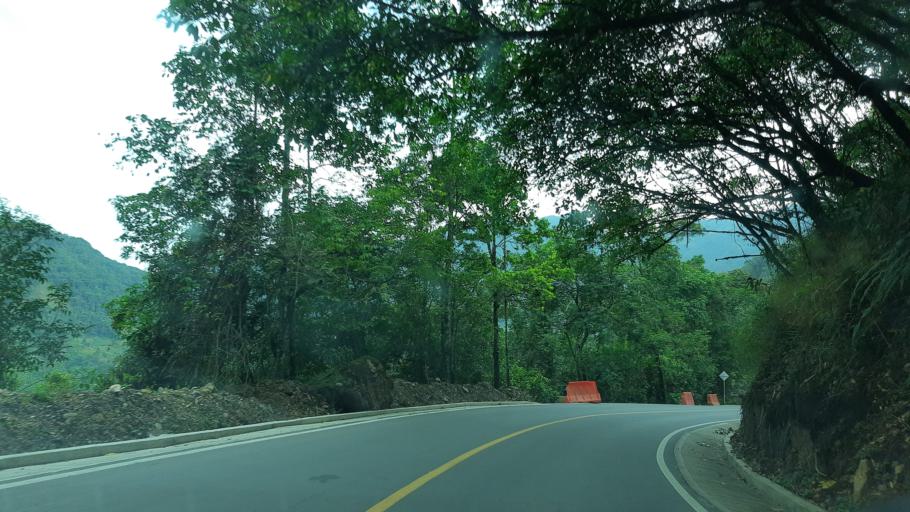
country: CO
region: Boyaca
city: Santa Maria
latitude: 4.8682
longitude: -73.2311
